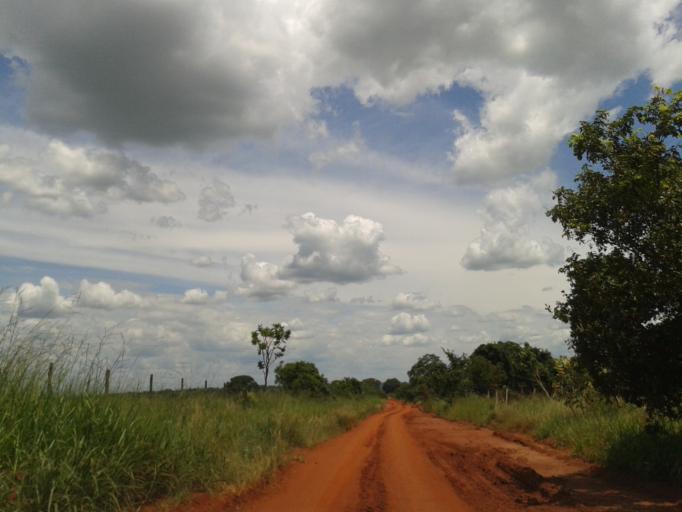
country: BR
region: Minas Gerais
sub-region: Ituiutaba
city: Ituiutaba
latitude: -18.8995
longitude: -49.4579
